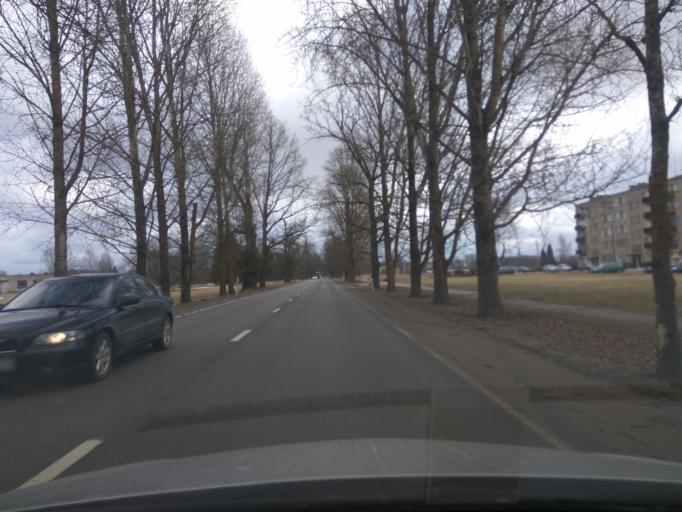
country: LV
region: Kuldigas Rajons
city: Kuldiga
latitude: 57.2761
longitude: 22.0253
